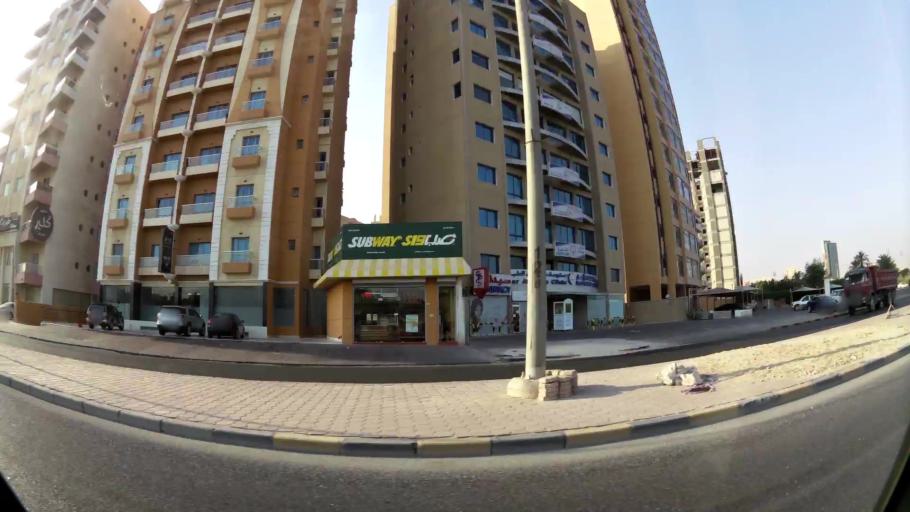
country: KW
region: Muhafazat Hawalli
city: Hawalli
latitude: 29.3431
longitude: 48.0370
